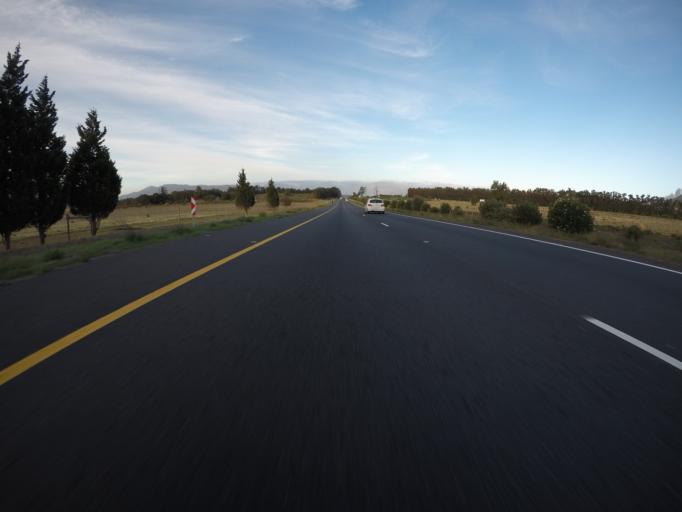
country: ZA
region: Western Cape
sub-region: City of Cape Town
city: Kraaifontein
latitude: -33.8085
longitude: 18.8318
